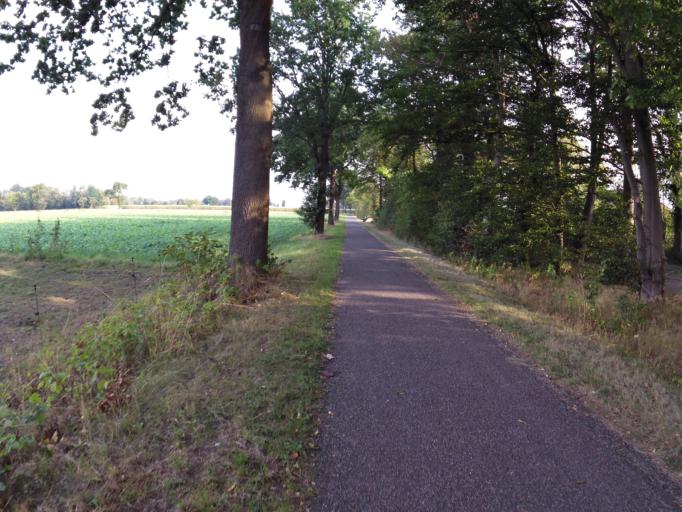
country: DE
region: North Rhine-Westphalia
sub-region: Regierungsbezirk Detmold
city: Petershagen
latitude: 52.3881
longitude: 8.9632
